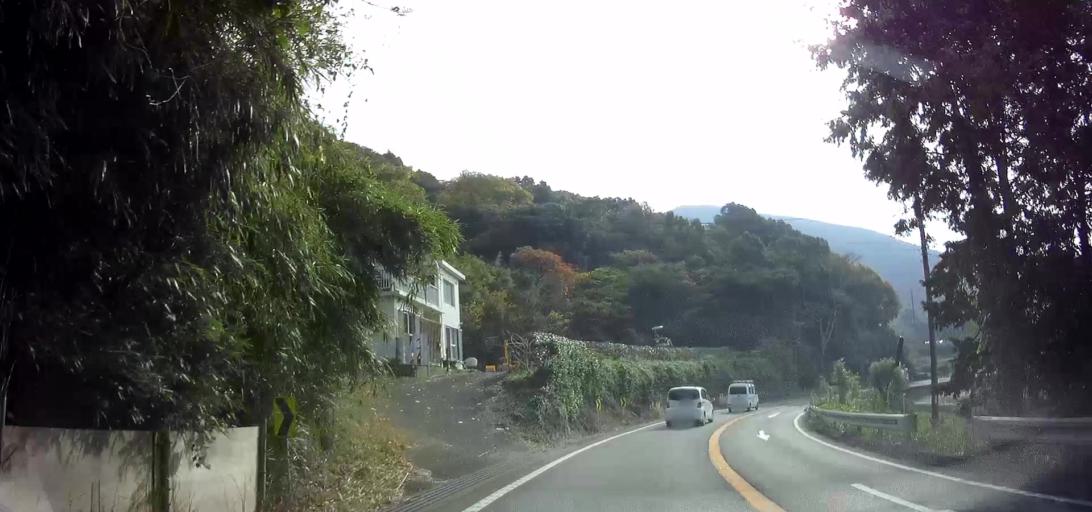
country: JP
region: Nagasaki
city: Shimabara
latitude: 32.7526
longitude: 130.2108
